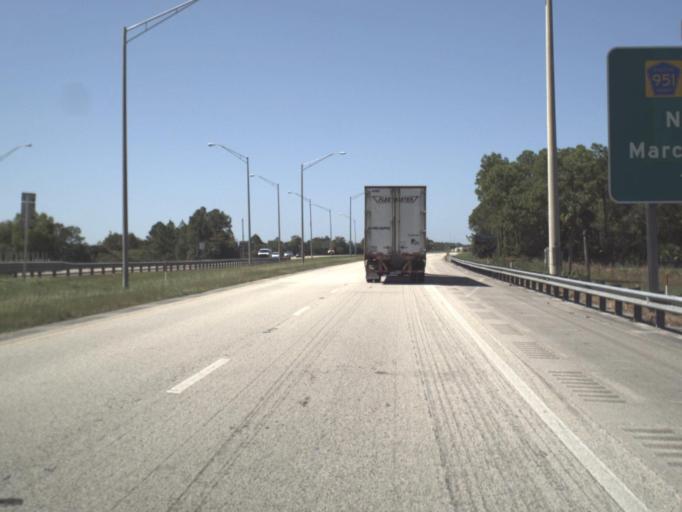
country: US
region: Florida
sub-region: Collier County
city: Golden Gate
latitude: 26.1558
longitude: -81.6685
